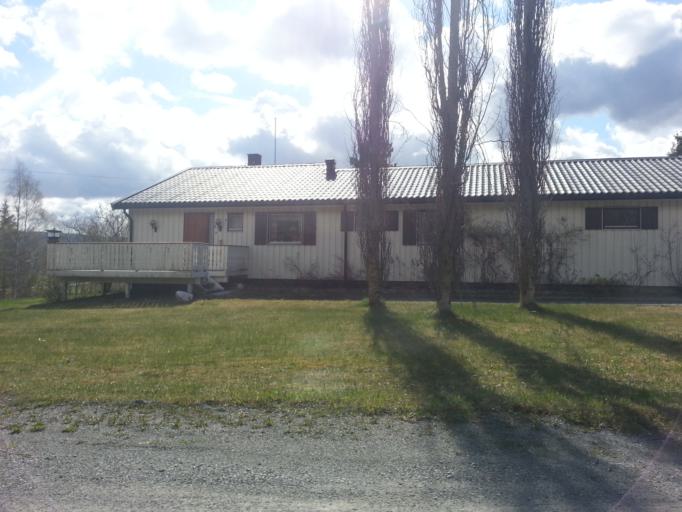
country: NO
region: Nord-Trondelag
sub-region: Levanger
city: Skogn
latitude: 63.6422
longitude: 11.2511
